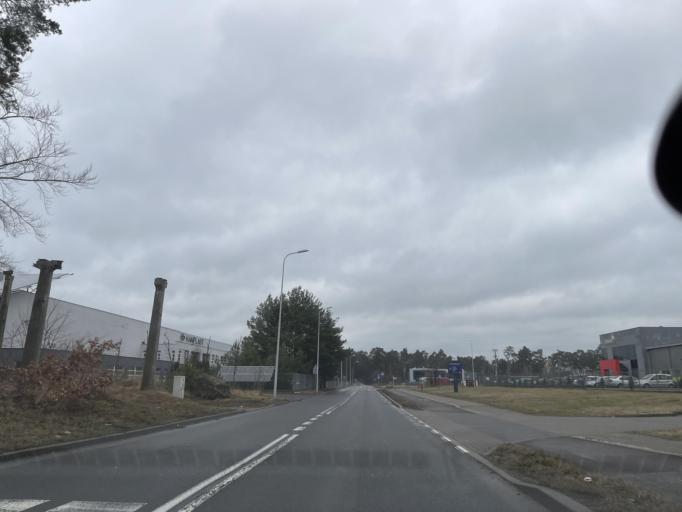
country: PL
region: Kujawsko-Pomorskie
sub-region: Bydgoszcz
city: Bydgoszcz
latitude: 53.0944
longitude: 18.0565
